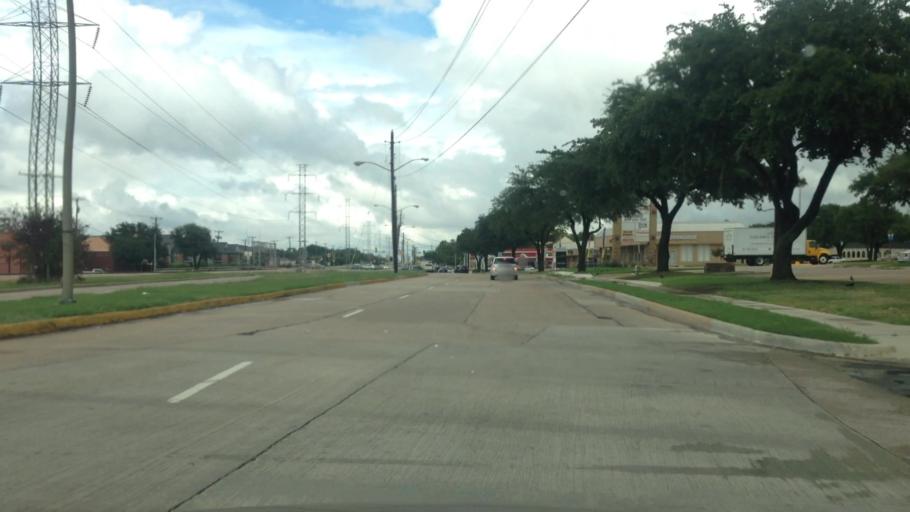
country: US
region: Texas
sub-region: Tarrant County
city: Edgecliff Village
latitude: 32.6576
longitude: -97.4018
